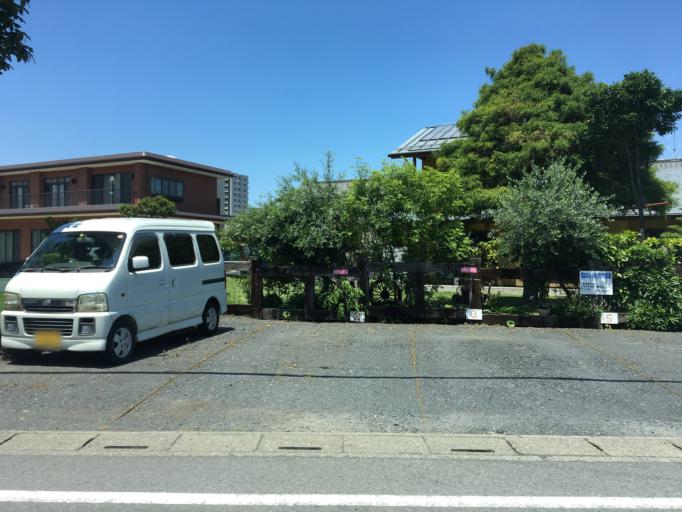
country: JP
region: Saitama
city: Sakado
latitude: 35.9451
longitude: 139.4054
